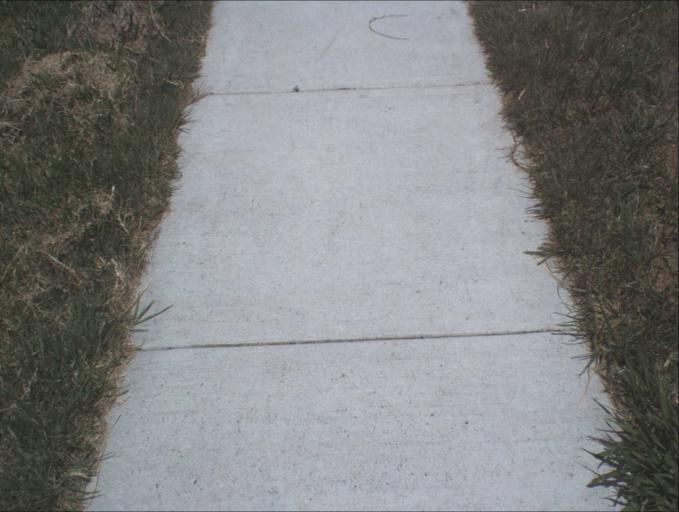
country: AU
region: Queensland
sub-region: Logan
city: Rochedale South
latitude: -27.5946
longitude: 153.1055
